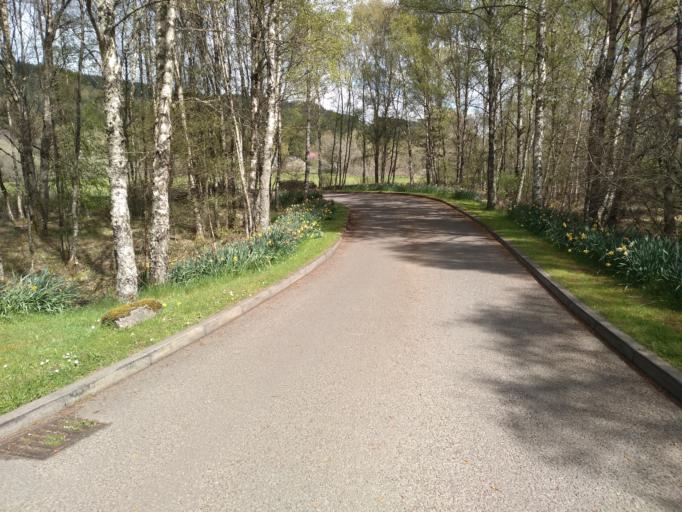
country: GB
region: Scotland
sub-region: Perth and Kinross
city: Aberfeldy
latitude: 56.7055
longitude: -4.0060
